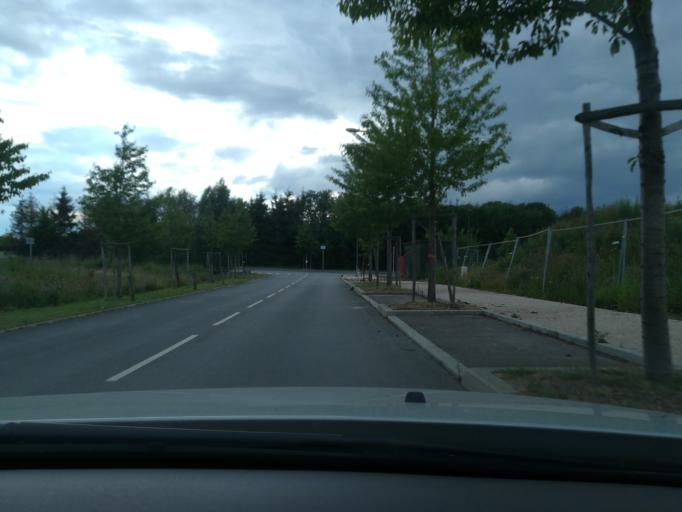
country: FR
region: Haute-Normandie
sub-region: Departement de la Seine-Maritime
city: Isneauville
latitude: 49.4894
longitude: 1.1362
